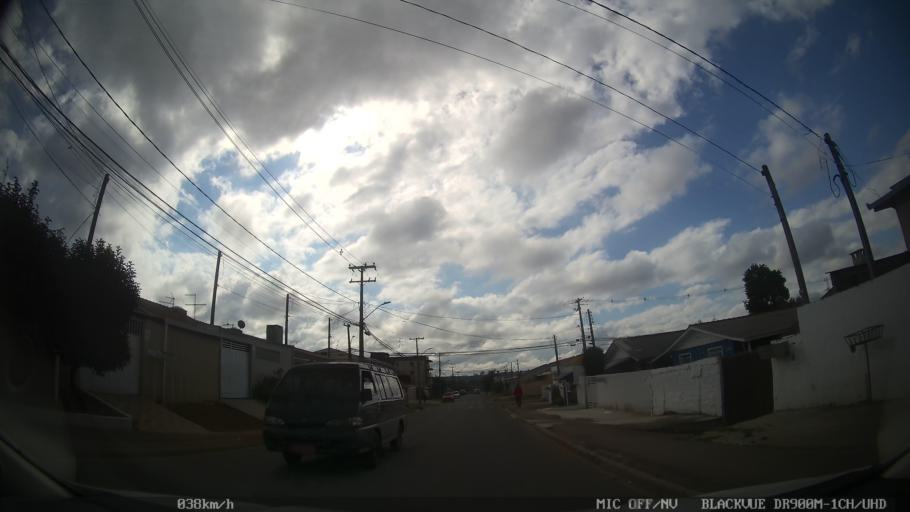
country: BR
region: Parana
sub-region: Colombo
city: Colombo
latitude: -25.3480
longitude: -49.1939
